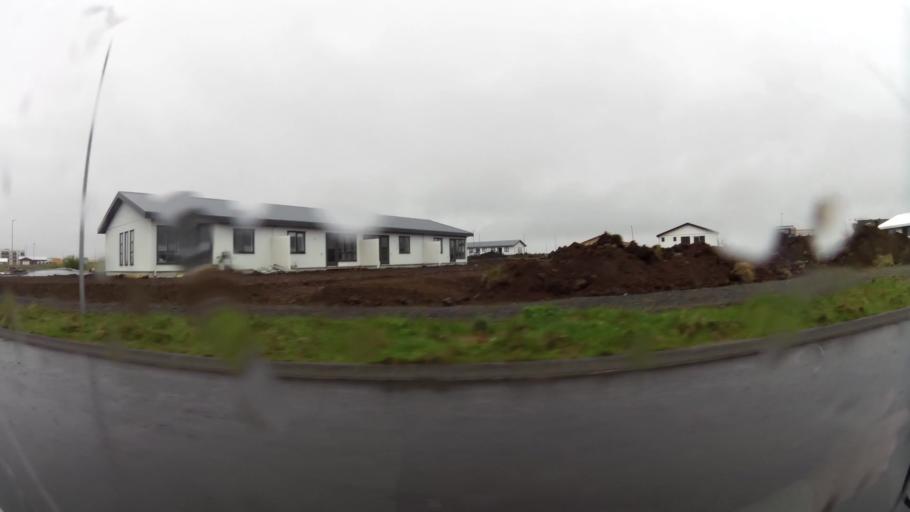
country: IS
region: South
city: Selfoss
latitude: 63.9297
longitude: -21.0285
